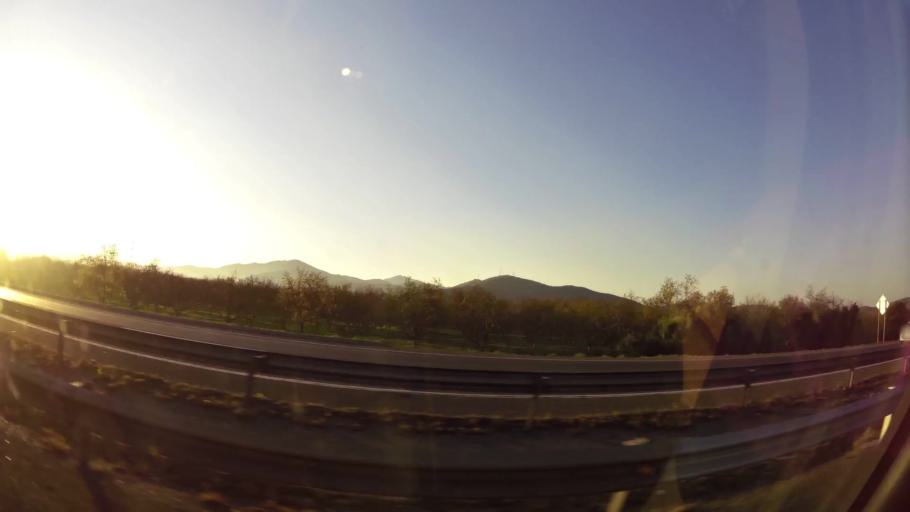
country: CL
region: Santiago Metropolitan
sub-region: Provincia de Talagante
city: Penaflor
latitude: -33.5636
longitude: -70.8411
